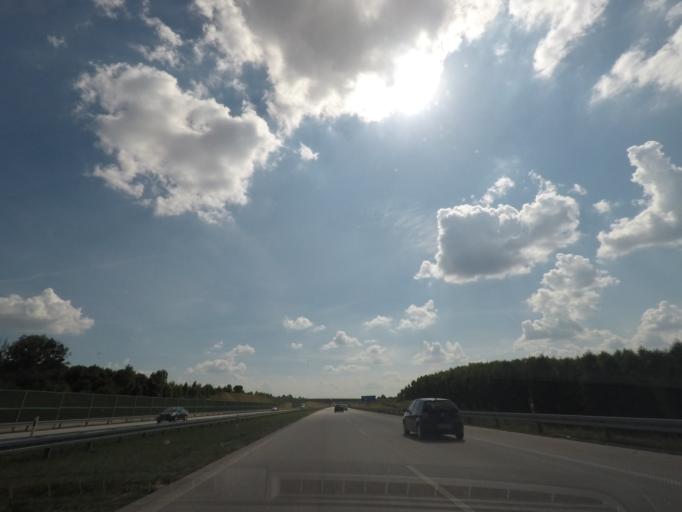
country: PL
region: Lodz Voivodeship
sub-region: Powiat zgierski
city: Strykow
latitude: 51.8244
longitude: 19.6493
